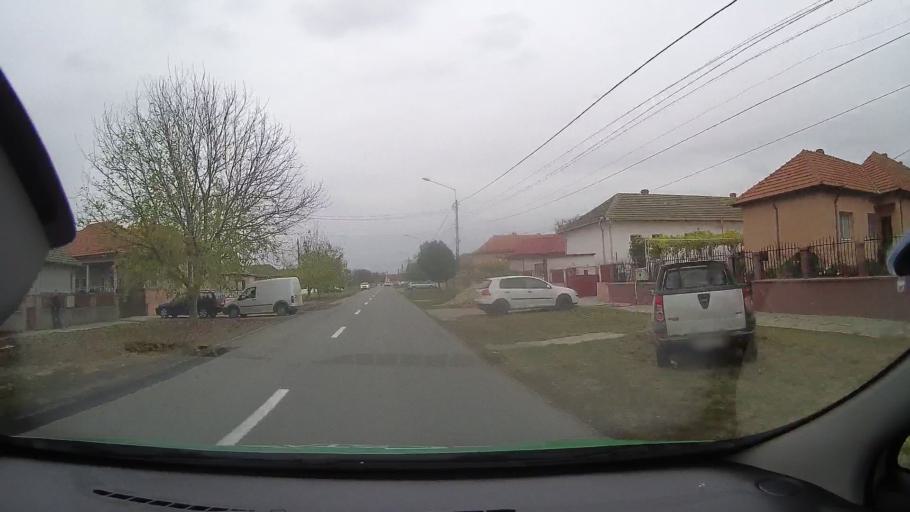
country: RO
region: Constanta
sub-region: Comuna Mihail Kogalniceanu
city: Mihail Kogalniceanu
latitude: 44.3756
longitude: 28.4649
